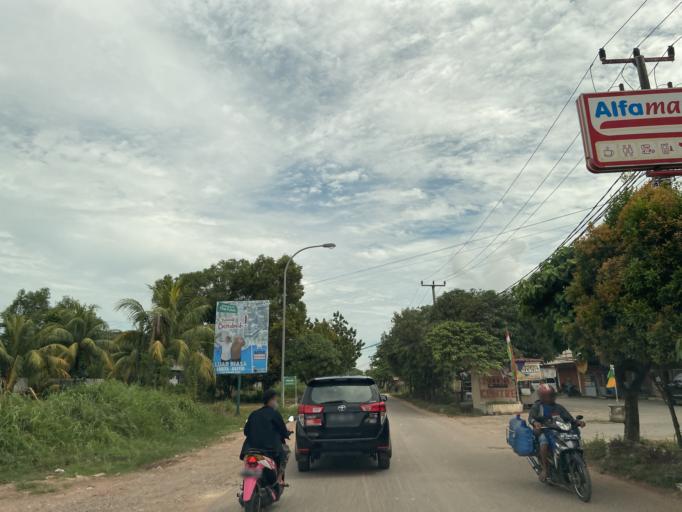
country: SG
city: Singapore
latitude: 1.0421
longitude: 103.9773
